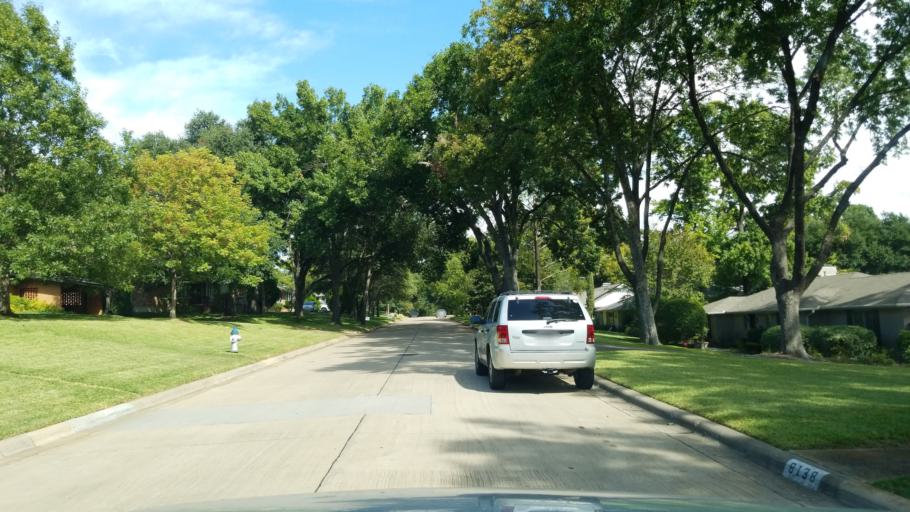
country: US
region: Texas
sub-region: Dallas County
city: Highland Park
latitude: 32.8087
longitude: -96.7176
